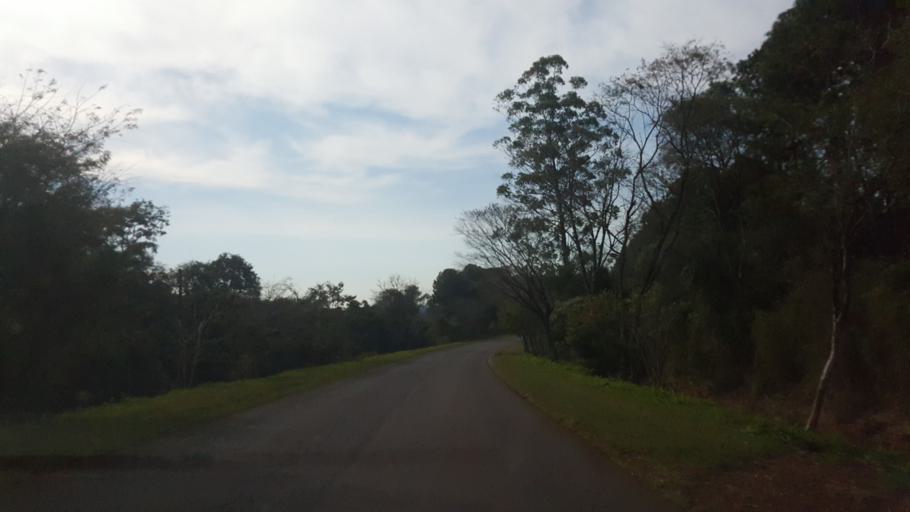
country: AR
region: Misiones
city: Capiovi
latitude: -26.9332
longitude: -55.0881
